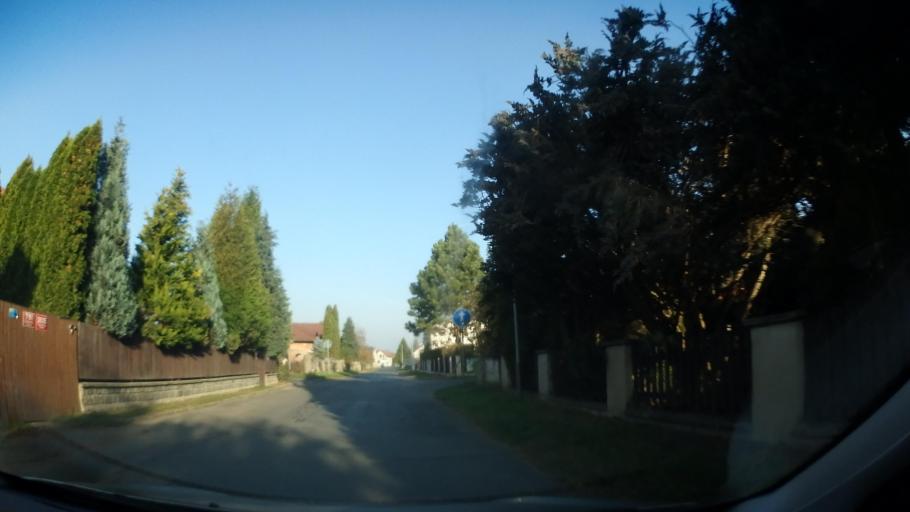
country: CZ
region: Central Bohemia
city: Sestajovice
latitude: 50.0706
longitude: 14.6756
